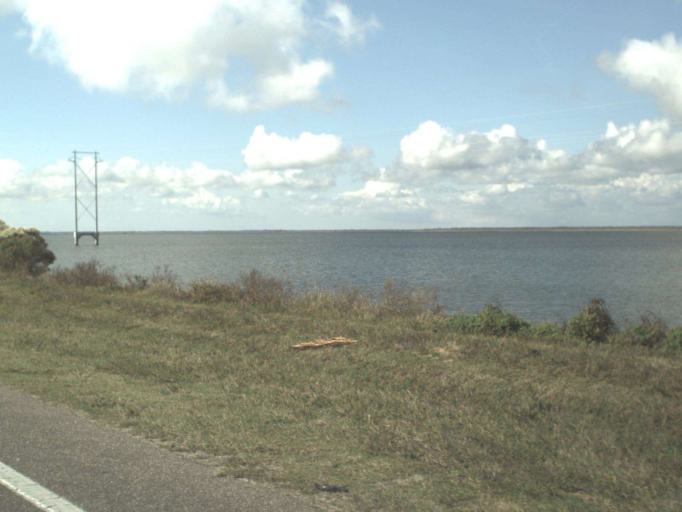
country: US
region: Florida
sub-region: Franklin County
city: Eastpoint
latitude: 29.7352
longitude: -84.9035
